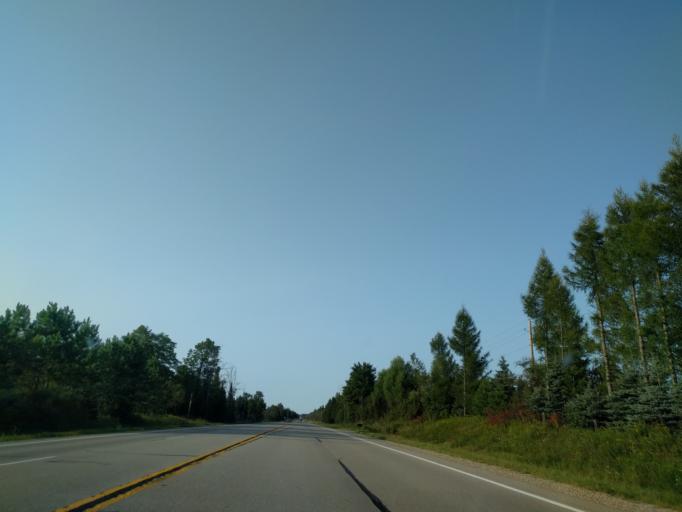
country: US
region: Michigan
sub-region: Delta County
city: Gladstone
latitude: 46.0946
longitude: -86.9808
